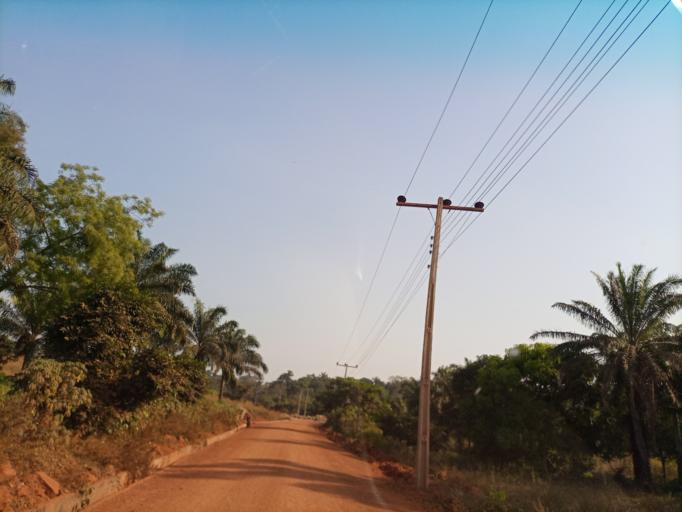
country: NG
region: Enugu
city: Opi
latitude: 6.7680
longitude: 7.3932
